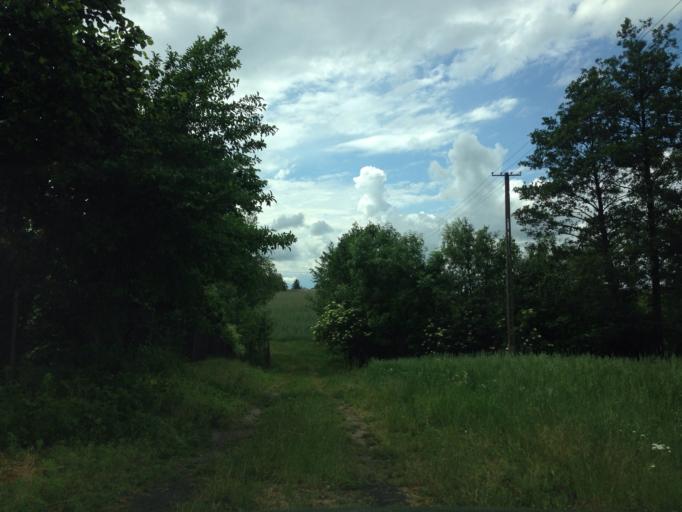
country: PL
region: Kujawsko-Pomorskie
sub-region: Powiat brodnicki
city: Gorzno
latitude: 53.1925
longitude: 19.5964
